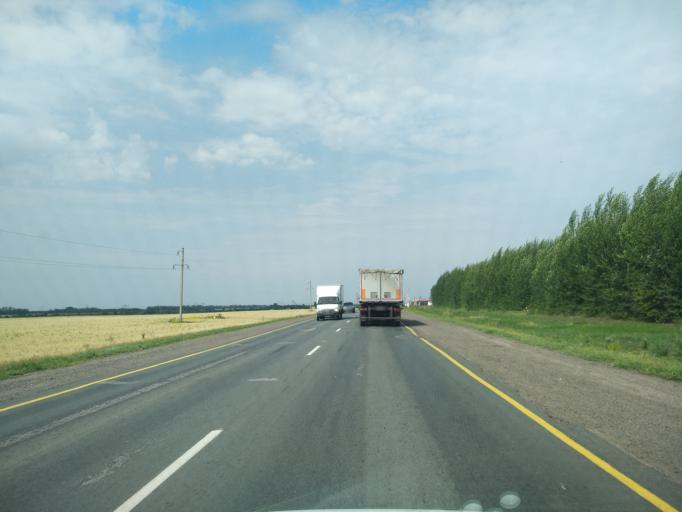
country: RU
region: Voronezj
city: Orlovo
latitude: 51.6771
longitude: 39.6893
